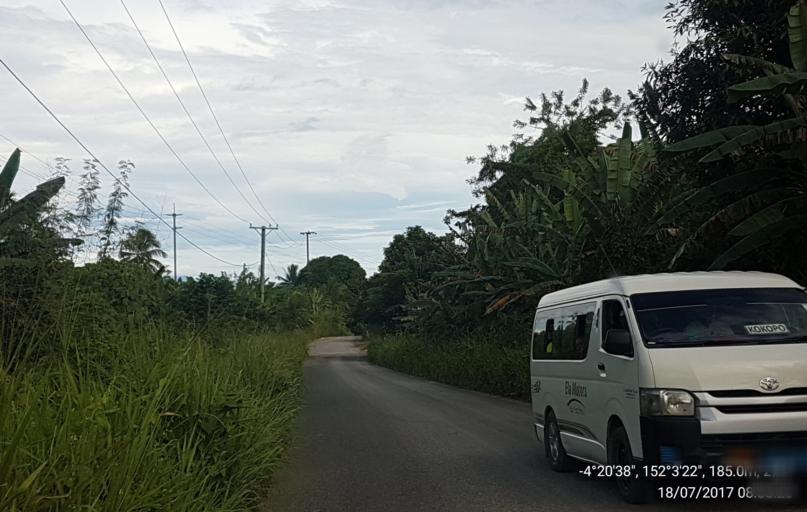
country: PG
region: East New Britain
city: Rabaul
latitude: -4.3442
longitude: 152.0567
